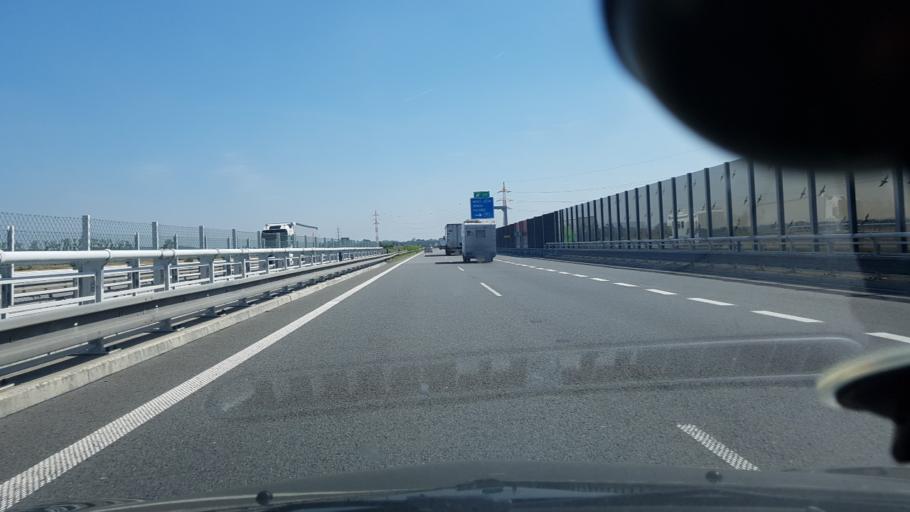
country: CZ
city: Fulnek
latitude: 49.6902
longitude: 17.9563
